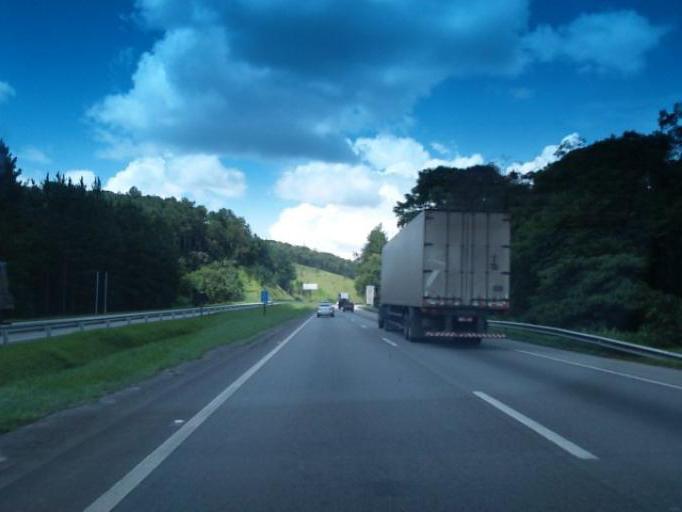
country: BR
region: Sao Paulo
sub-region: Juquitiba
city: Juquitiba
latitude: -23.9703
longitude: -47.1345
